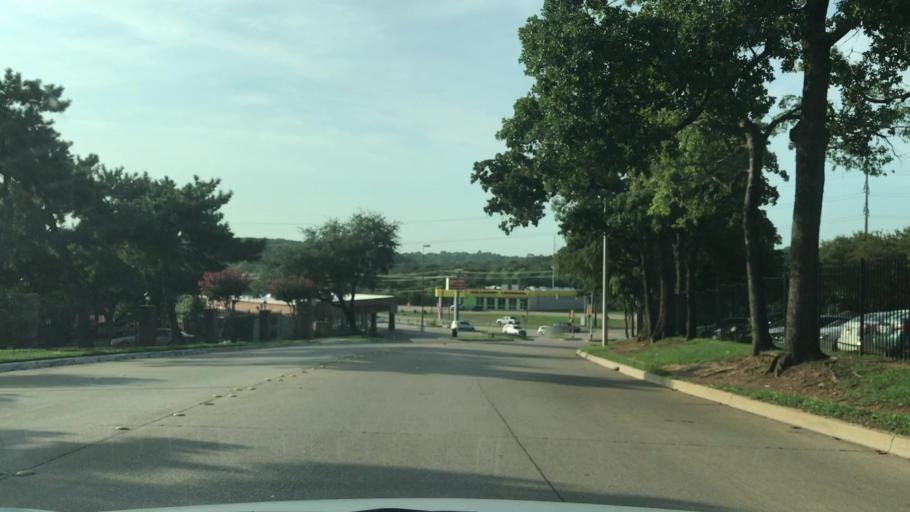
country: US
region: Texas
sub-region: Tarrant County
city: Pantego
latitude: 32.7589
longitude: -97.1570
